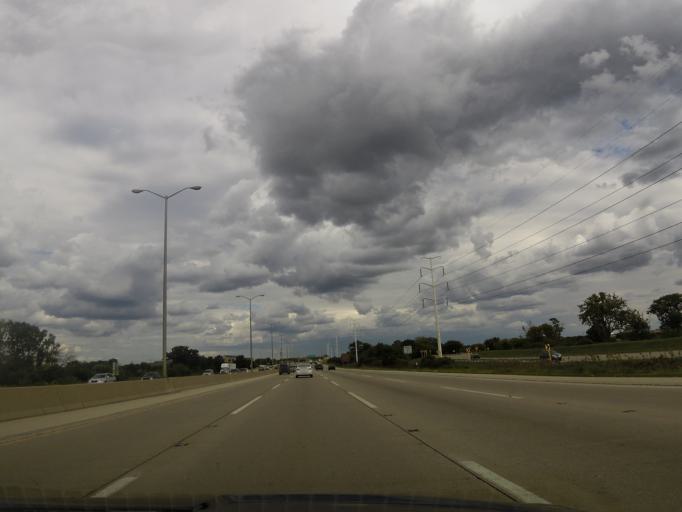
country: US
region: Illinois
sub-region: DuPage County
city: Warrenville
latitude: 41.8055
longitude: -88.1809
